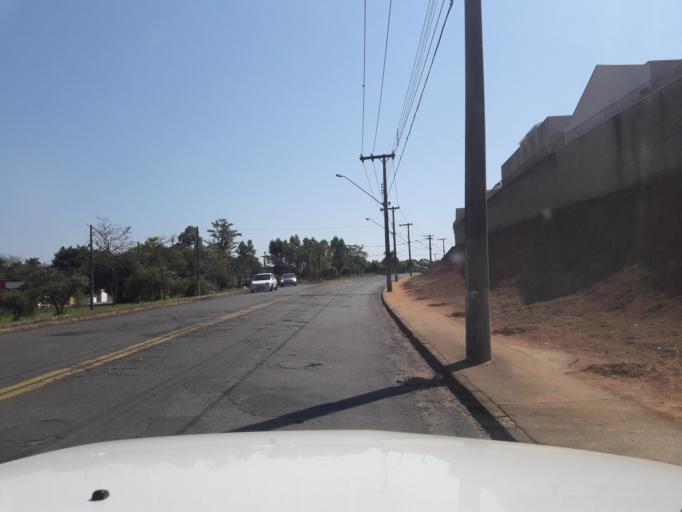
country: BR
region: Sao Paulo
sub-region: Moji-Guacu
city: Mogi-Gaucu
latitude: -22.3564
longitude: -46.9575
